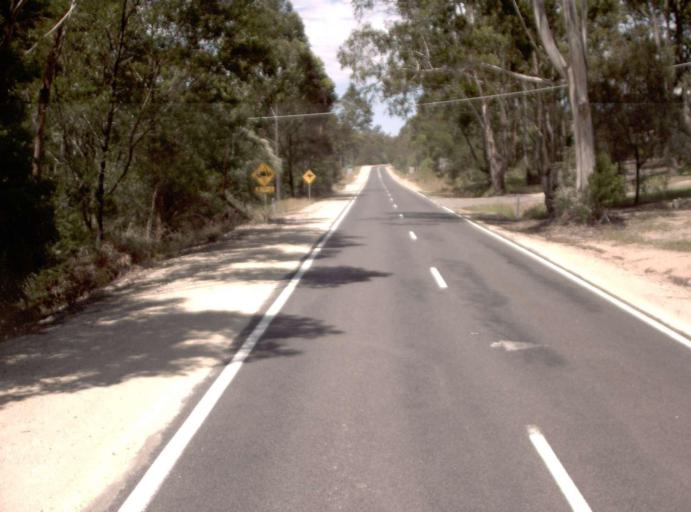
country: AU
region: New South Wales
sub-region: Bombala
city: Bombala
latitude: -37.5642
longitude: 149.1569
